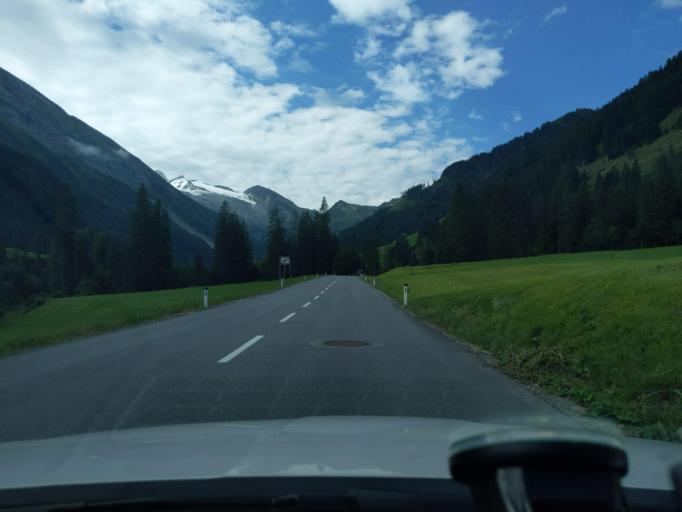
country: AT
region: Tyrol
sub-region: Politischer Bezirk Innsbruck Land
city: Schmirn
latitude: 47.1365
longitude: 11.7061
